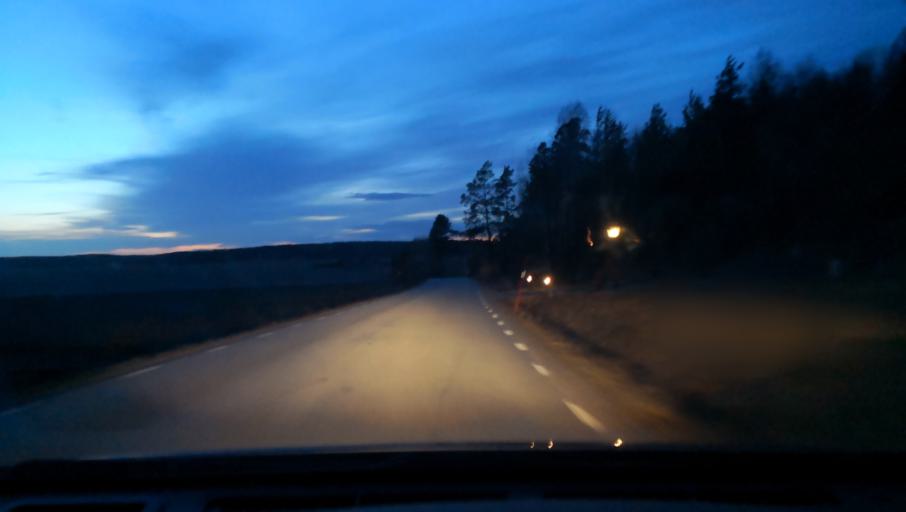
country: SE
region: Uppsala
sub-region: Enkopings Kommun
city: Grillby
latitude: 59.6069
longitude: 17.2800
